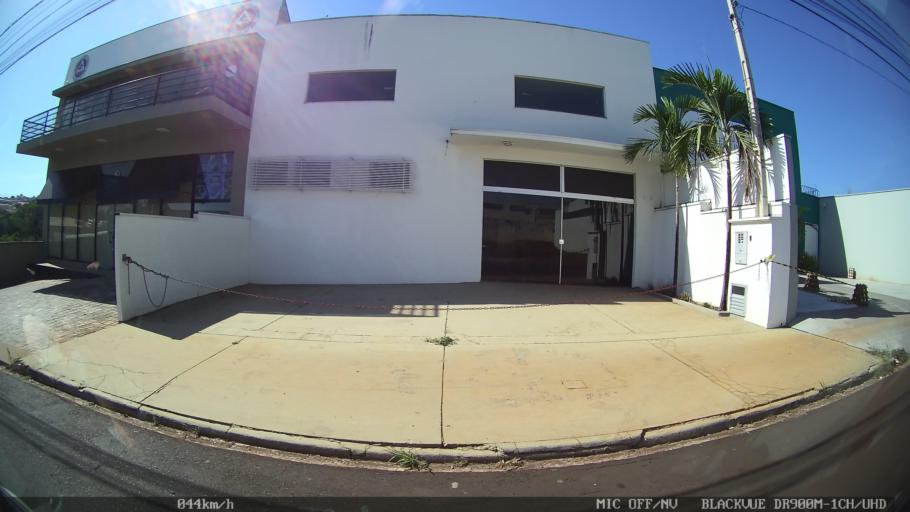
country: BR
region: Sao Paulo
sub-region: Batatais
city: Batatais
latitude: -20.8869
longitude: -47.5827
